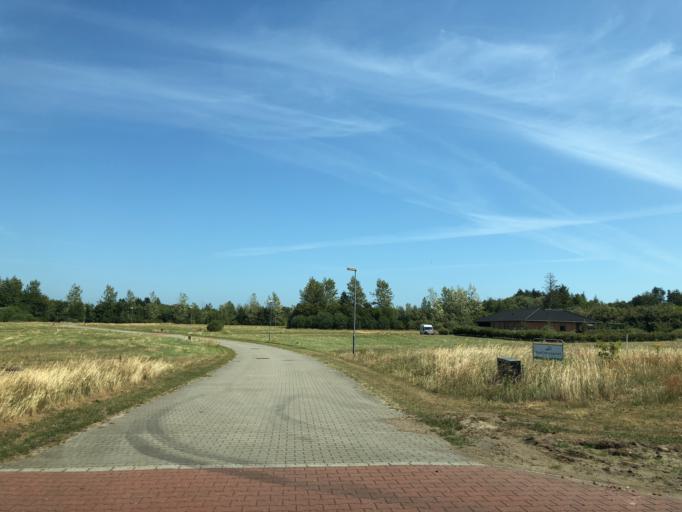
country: DK
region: Central Jutland
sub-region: Holstebro Kommune
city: Ulfborg
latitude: 56.2670
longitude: 8.3102
